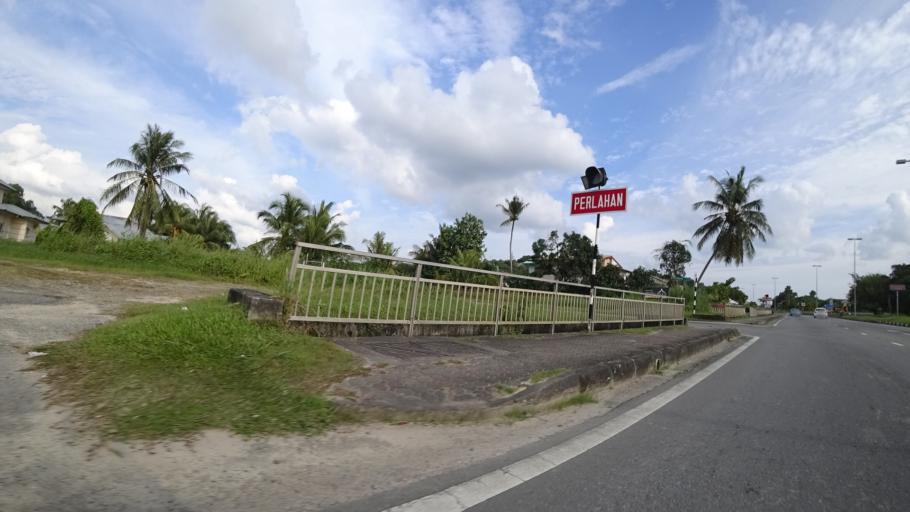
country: BN
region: Brunei and Muara
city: Bandar Seri Begawan
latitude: 4.8746
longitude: 114.8609
